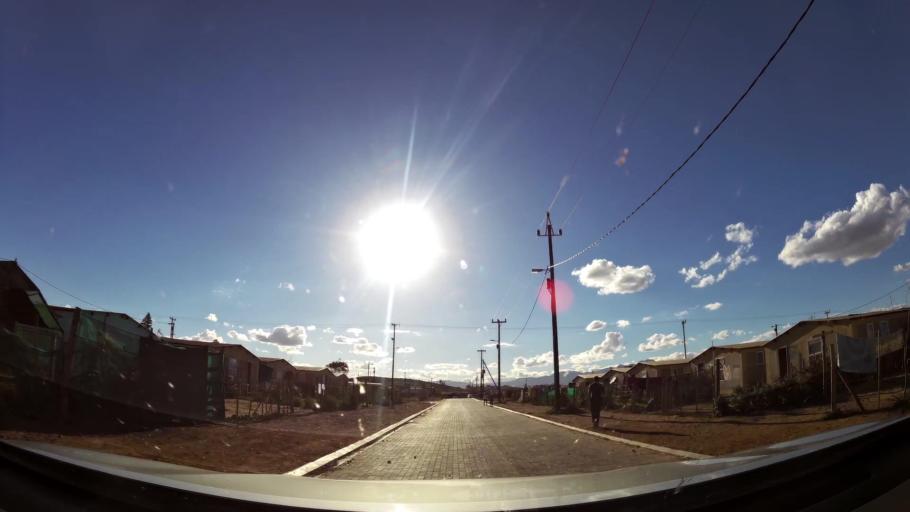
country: ZA
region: Western Cape
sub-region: Eden District Municipality
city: Riversdale
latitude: -34.1092
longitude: 20.9638
